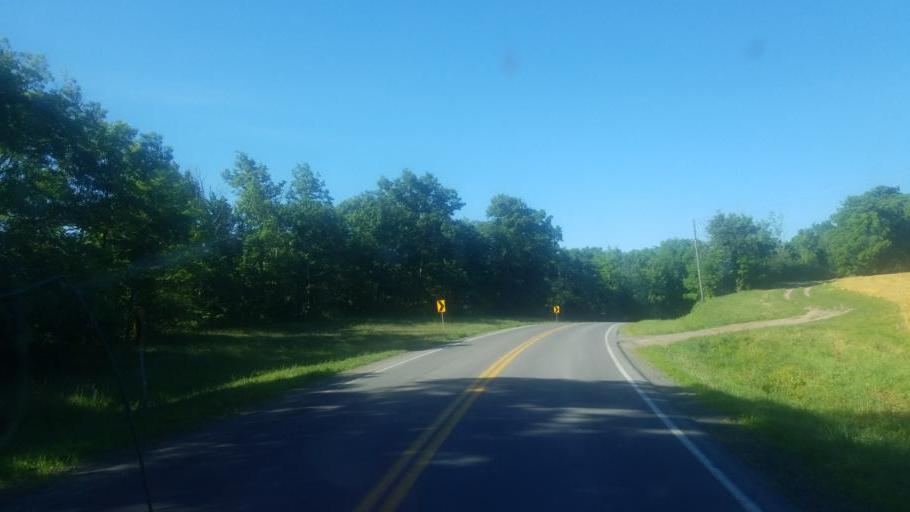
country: US
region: New York
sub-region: Ontario County
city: Clifton Springs
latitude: 42.8451
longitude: -77.1086
